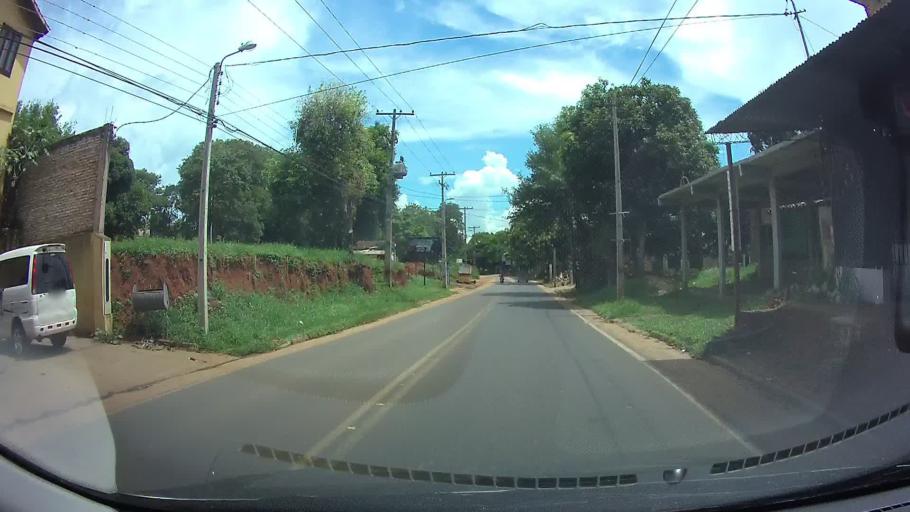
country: PY
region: Central
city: San Lorenzo
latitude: -25.3034
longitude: -57.4911
